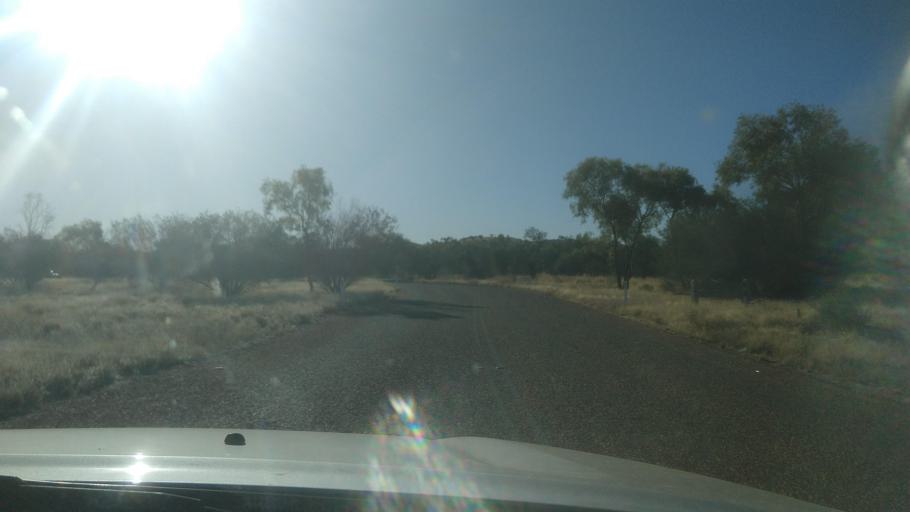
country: AU
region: Northern Territory
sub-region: Alice Springs
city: Alice Springs
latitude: -23.7012
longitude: 133.8297
